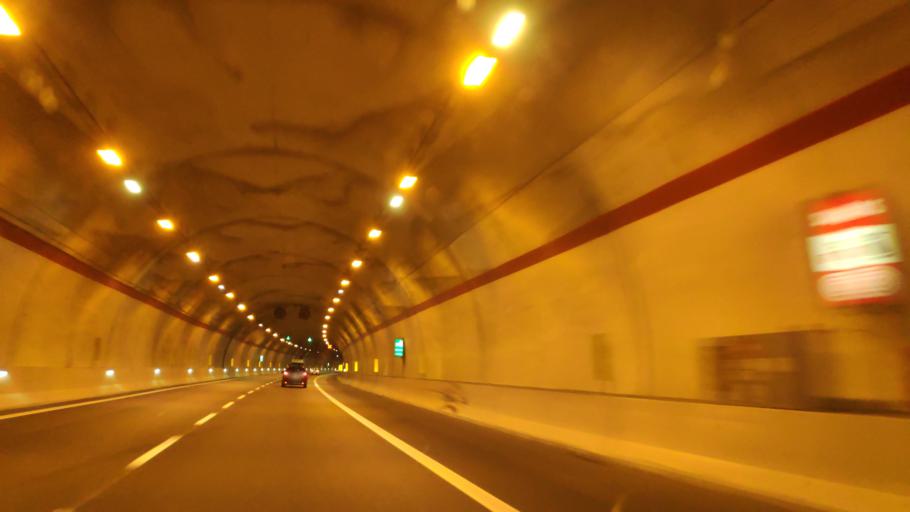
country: IT
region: Calabria
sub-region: Provincia di Cosenza
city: Mormanno
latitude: 39.8815
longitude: 15.9846
